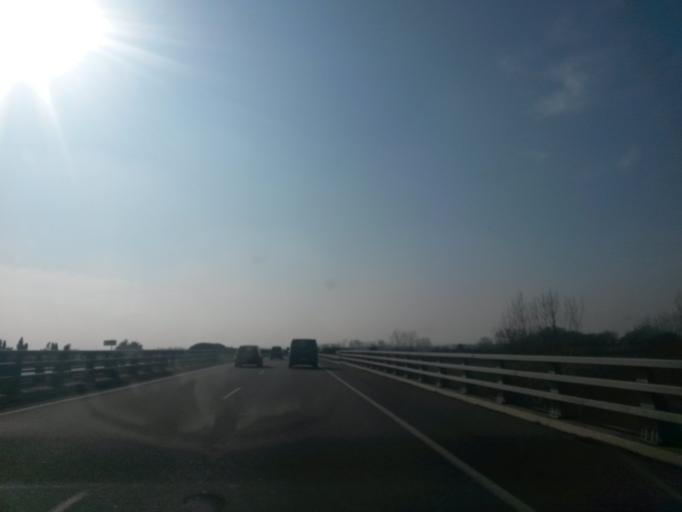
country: ES
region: Catalonia
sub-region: Provincia de Girona
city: Castello d'Empuries
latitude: 42.2549
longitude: 3.0866
